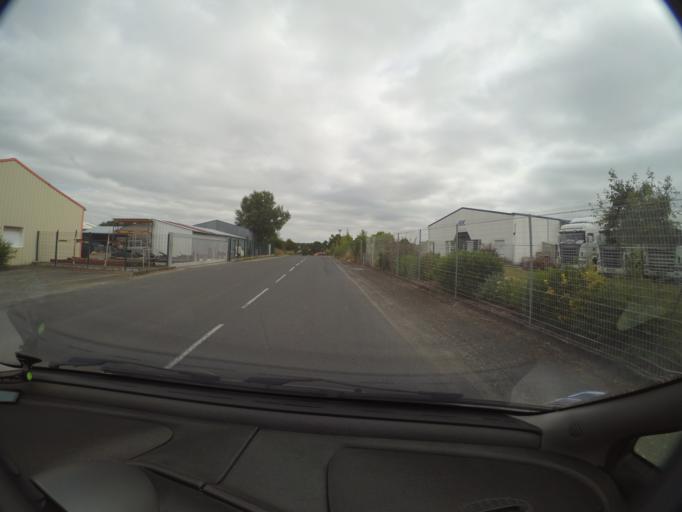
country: FR
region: Pays de la Loire
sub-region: Departement de la Vendee
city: Saint-Hilaire-de-Loulay
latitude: 47.0021
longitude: -1.3388
